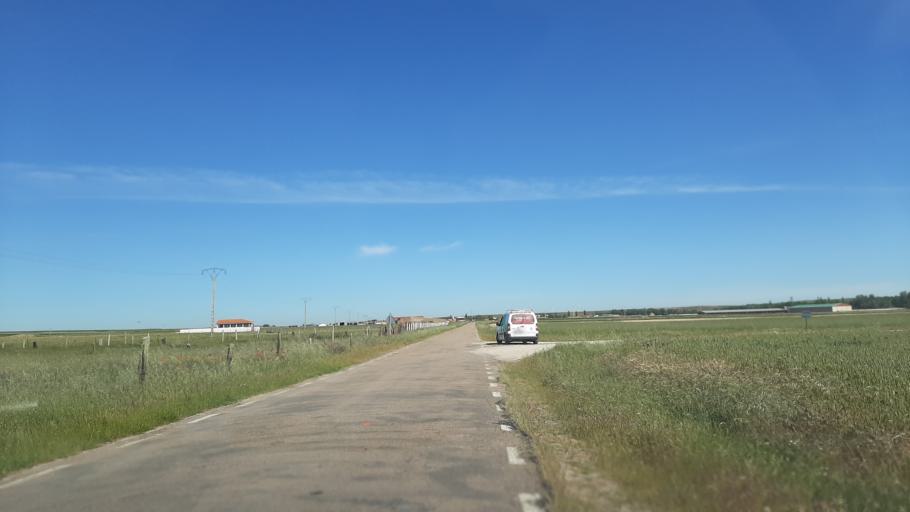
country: ES
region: Castille and Leon
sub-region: Provincia de Salamanca
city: Pedrosillo de Alba
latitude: 40.8123
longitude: -5.3853
